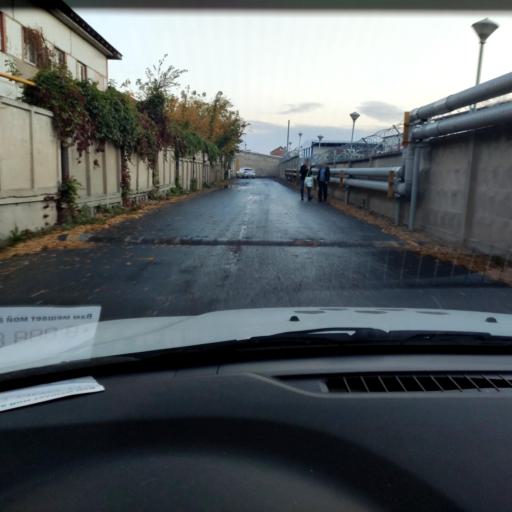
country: RU
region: Samara
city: Tol'yatti
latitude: 53.5468
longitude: 49.4366
